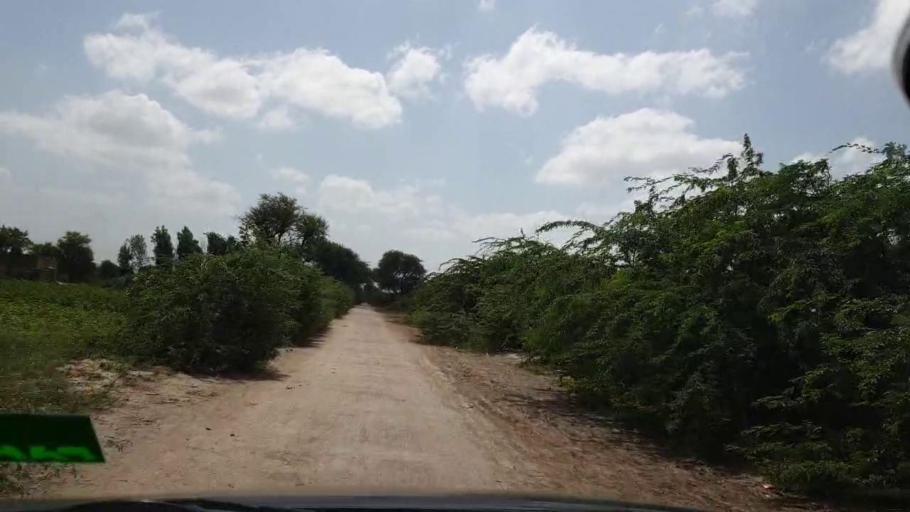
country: PK
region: Sindh
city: Kadhan
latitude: 24.5623
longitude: 69.2112
